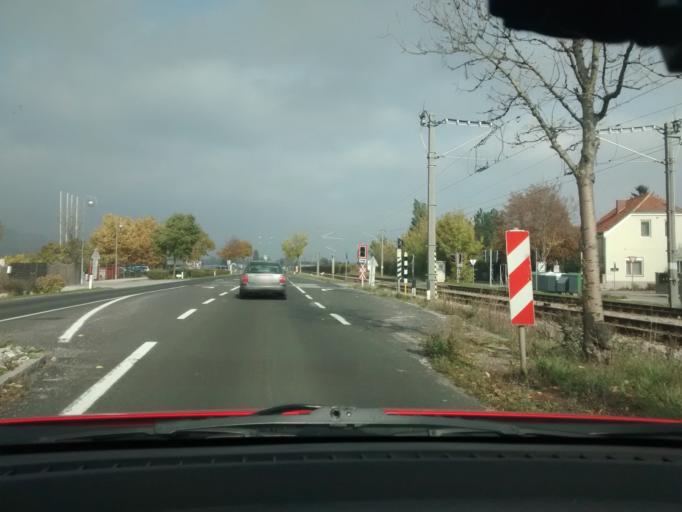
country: AT
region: Lower Austria
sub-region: Politischer Bezirk Baden
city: Traiskirchen
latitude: 48.0285
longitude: 16.3003
